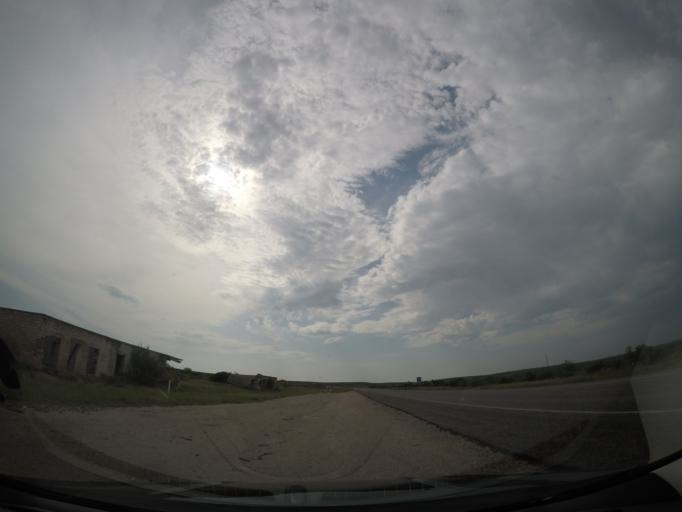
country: US
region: Texas
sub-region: Val Verde County
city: Cienegas Terrace
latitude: 29.7806
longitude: -101.3976
